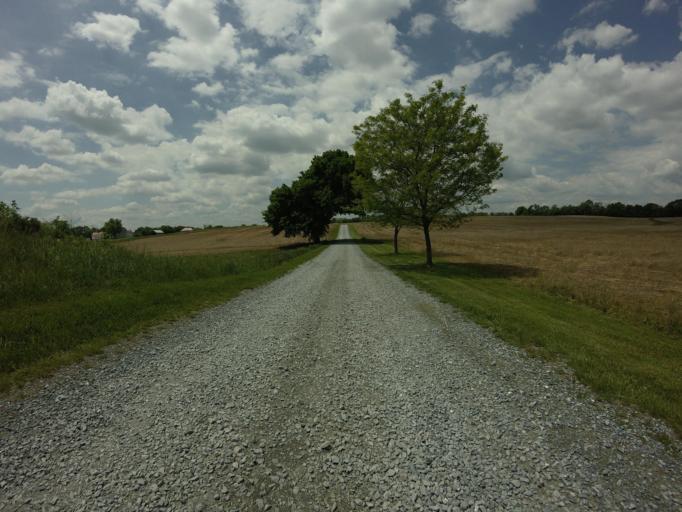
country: US
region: Maryland
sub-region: Frederick County
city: Ballenger Creek
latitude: 39.3729
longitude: -77.3962
